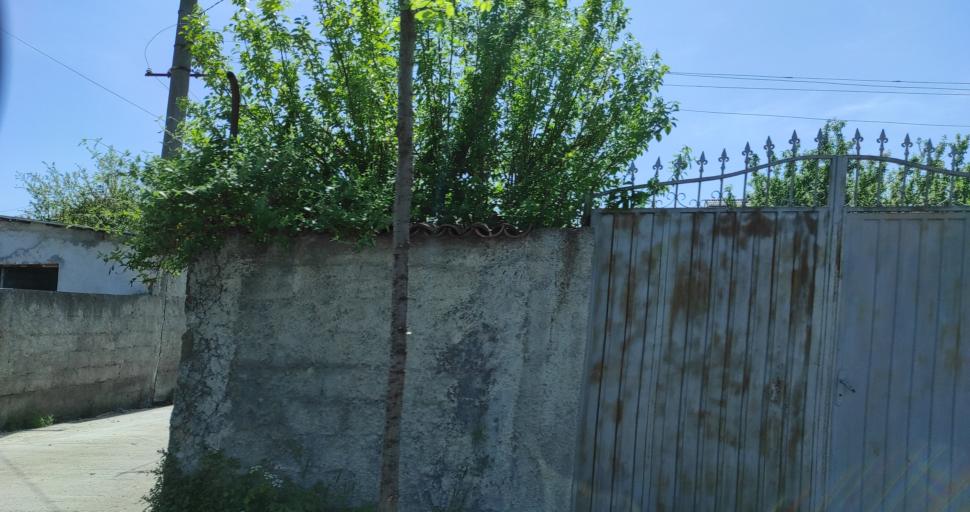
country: AL
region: Shkoder
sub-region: Rrethi i Shkodres
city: Shkoder
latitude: 42.1009
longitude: 19.5485
